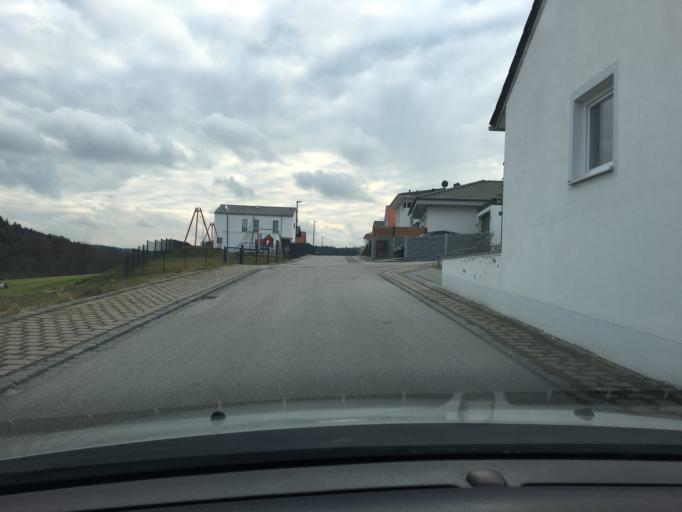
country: DE
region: Bavaria
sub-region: Lower Bavaria
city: Eching
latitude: 48.4940
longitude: 12.0630
